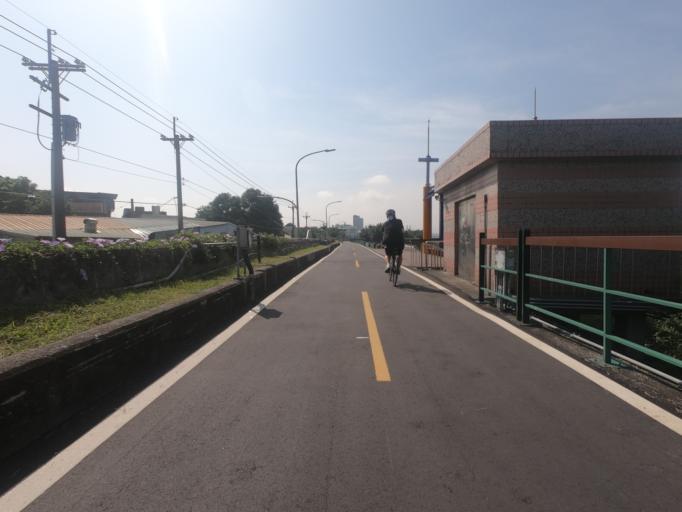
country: TW
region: Taipei
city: Taipei
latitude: 25.0979
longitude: 121.4920
